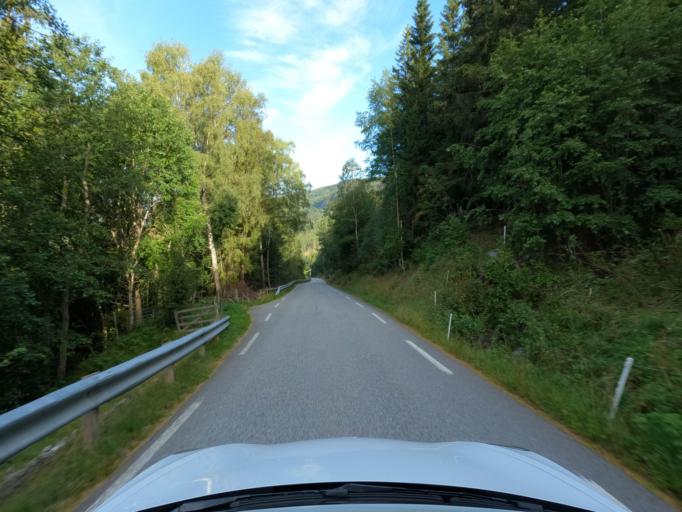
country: NO
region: Buskerud
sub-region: Nore og Uvdal
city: Rodberg
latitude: 60.0449
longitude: 8.8269
